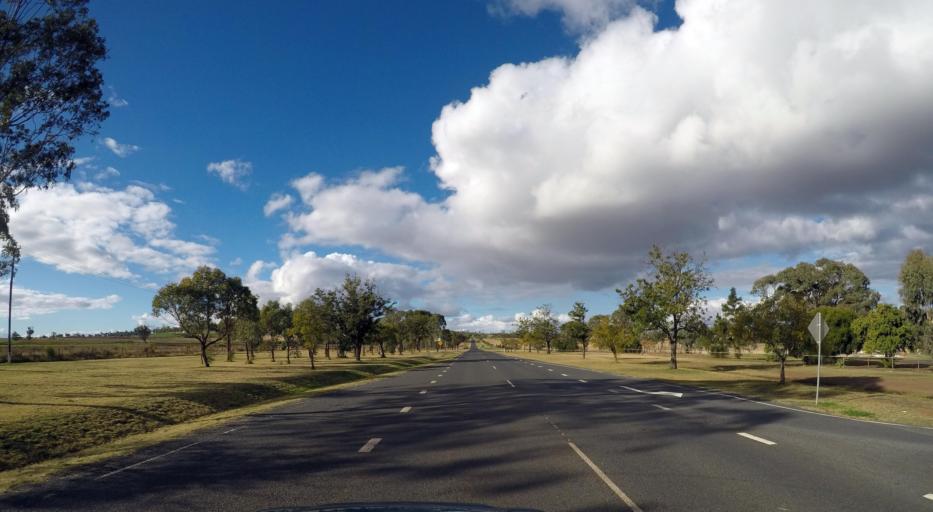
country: AU
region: Queensland
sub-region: Toowoomba
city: Westbrook
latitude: -27.7088
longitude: 151.6453
